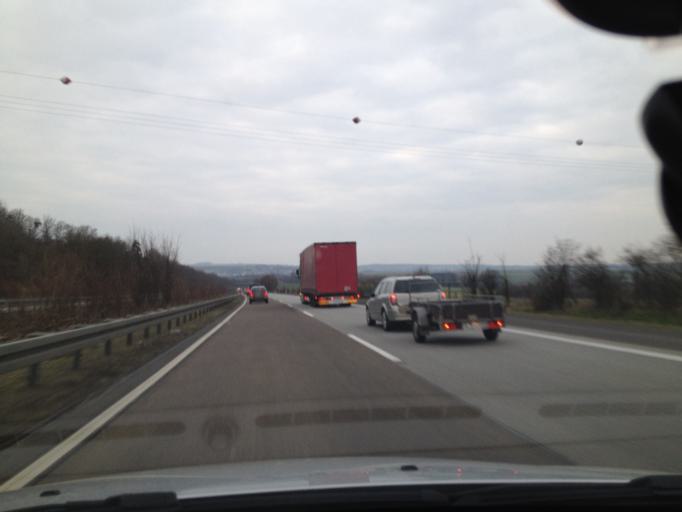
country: DE
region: Hesse
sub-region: Regierungsbezirk Darmstadt
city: Munzenberg
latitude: 50.4535
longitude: 8.7891
